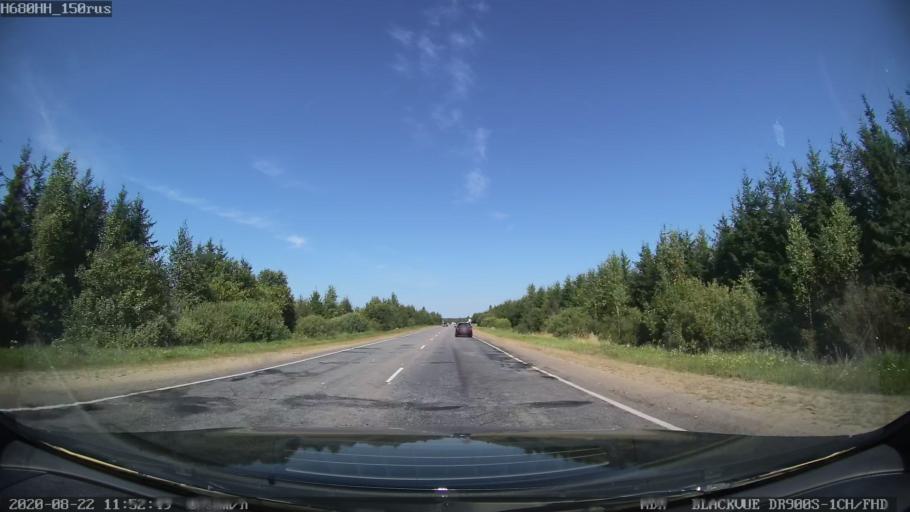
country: RU
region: Tverskaya
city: Vasil'yevskiy Mokh
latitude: 57.1199
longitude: 36.1146
